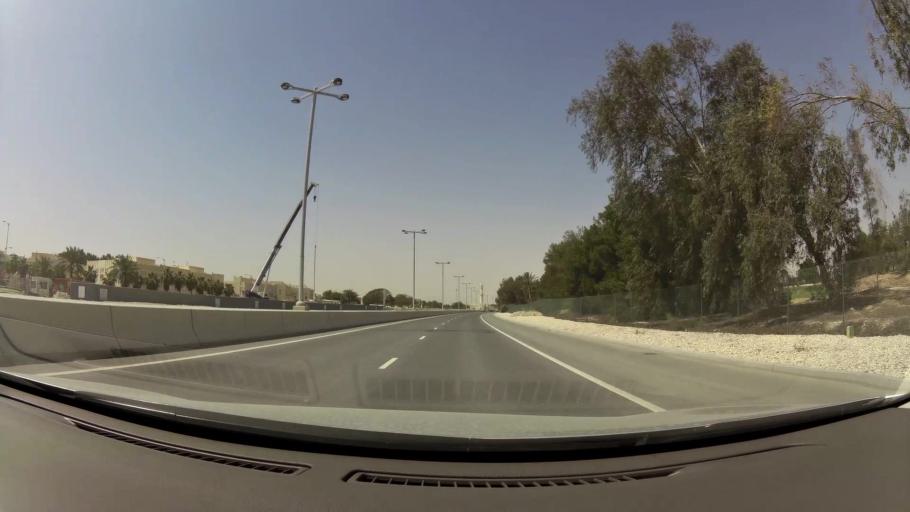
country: QA
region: Baladiyat ad Dawhah
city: Doha
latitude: 25.3789
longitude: 51.5150
